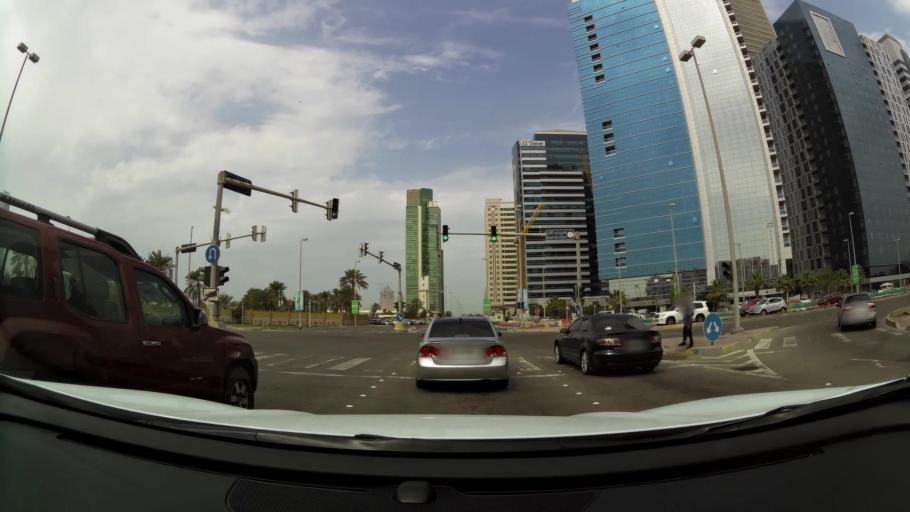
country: AE
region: Abu Dhabi
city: Abu Dhabi
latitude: 24.4669
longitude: 54.3400
